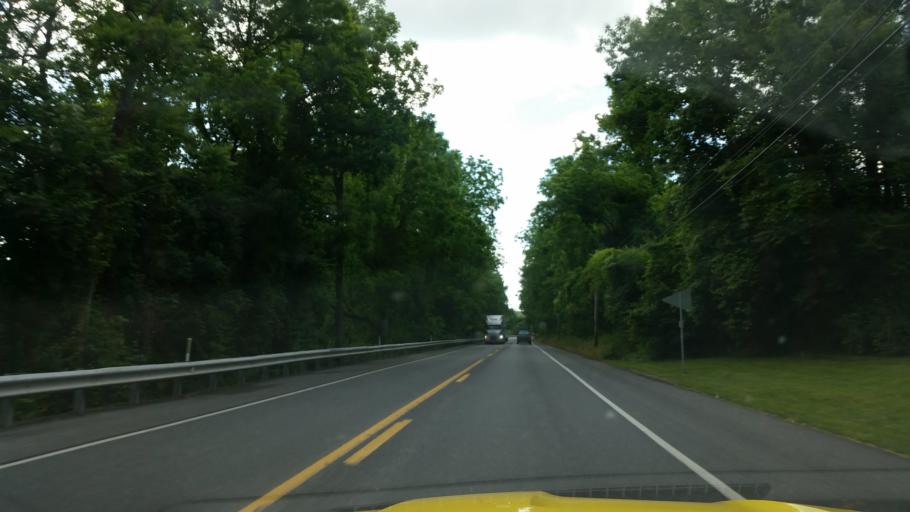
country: US
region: Pennsylvania
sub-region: Lancaster County
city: Brickerville
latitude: 40.2194
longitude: -76.3025
